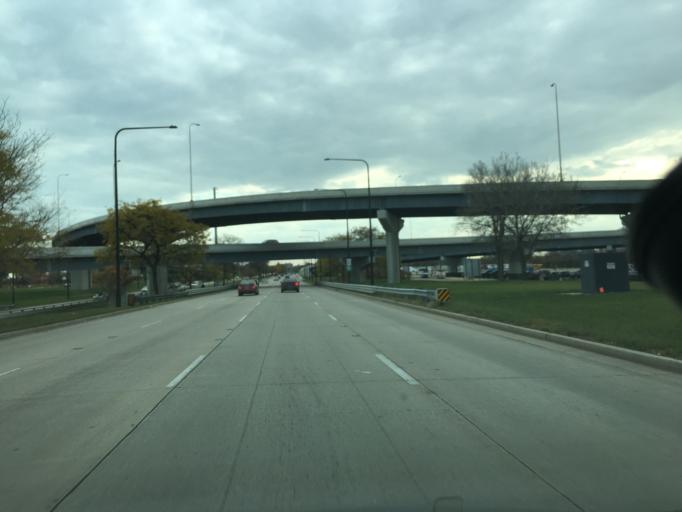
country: US
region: Illinois
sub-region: Cook County
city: Chicago
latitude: 41.8498
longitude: -87.6132
